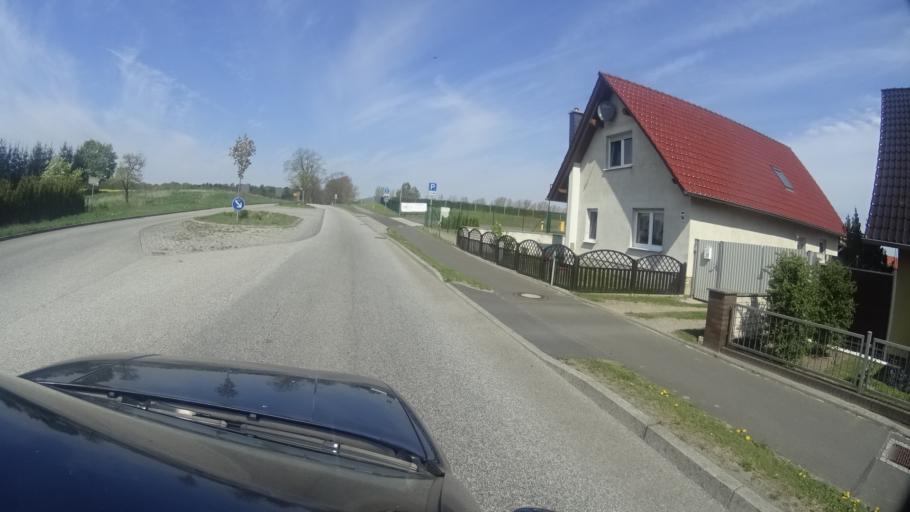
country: DE
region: Brandenburg
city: Retzow
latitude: 52.6248
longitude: 12.7506
